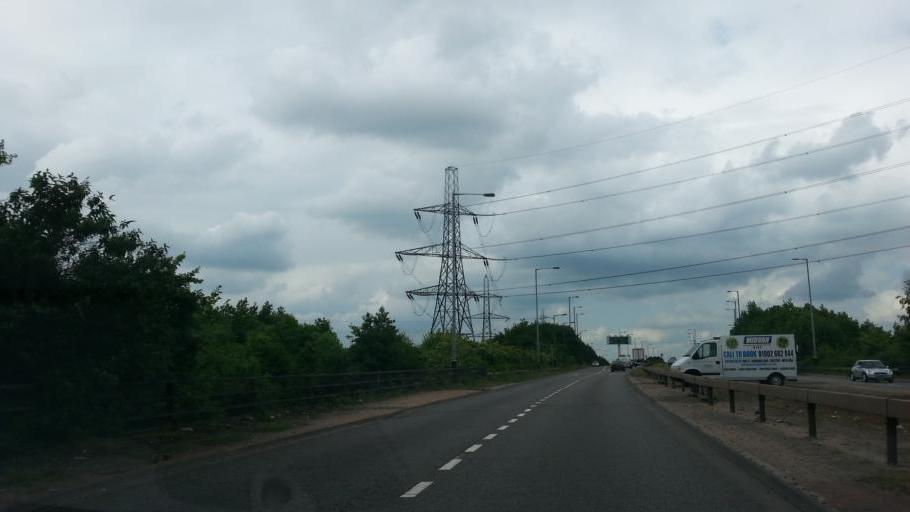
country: GB
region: England
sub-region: Walsall
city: Willenhall
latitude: 52.5722
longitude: -2.0512
